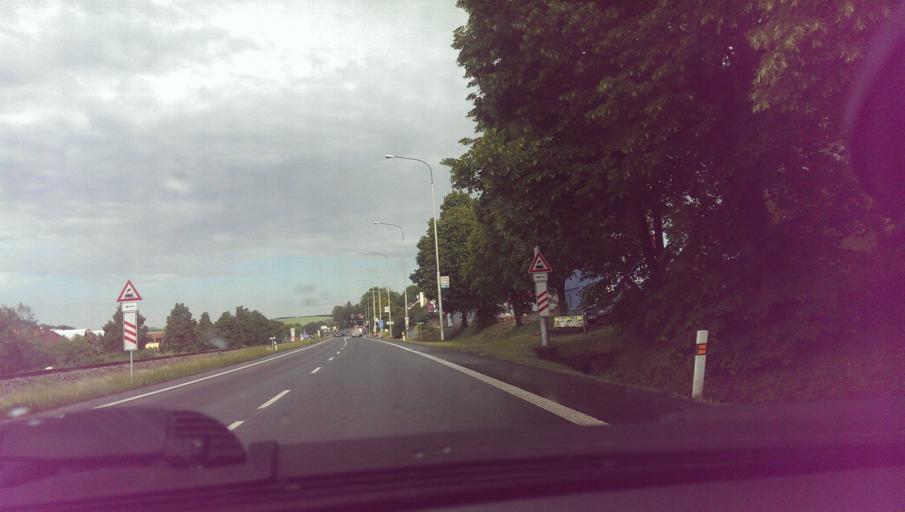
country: CZ
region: Zlin
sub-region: Okres Zlin
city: Zlin
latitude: 49.2207
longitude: 17.7112
